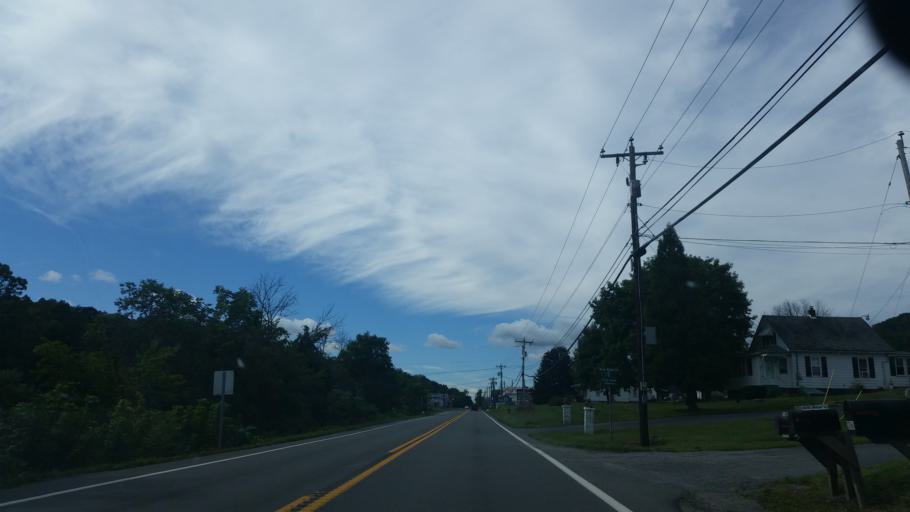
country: US
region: West Virginia
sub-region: Morgan County
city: Berkeley Springs
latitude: 39.5903
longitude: -78.2473
